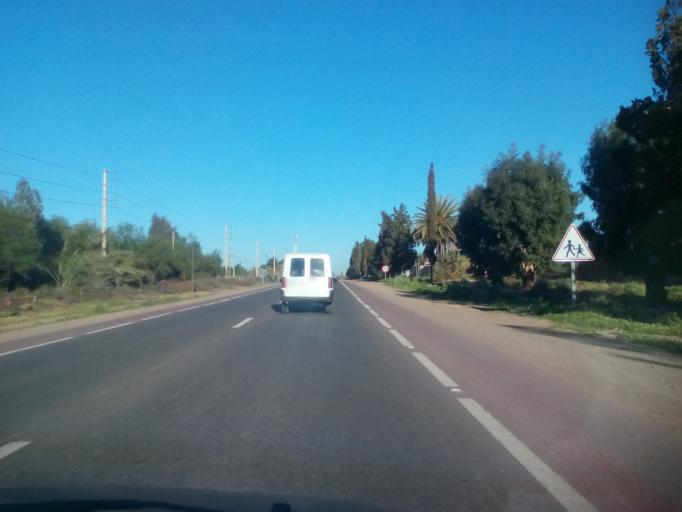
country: MA
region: Marrakech-Tensift-Al Haouz
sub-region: Marrakech
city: Marrakesh
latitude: 31.6316
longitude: -8.1855
